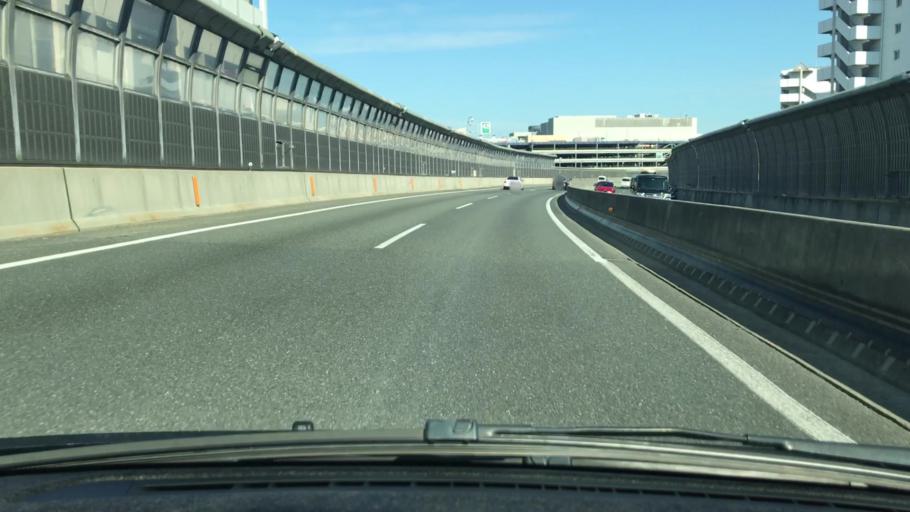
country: JP
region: Hyogo
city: Nishinomiya-hama
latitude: 34.7399
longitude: 135.3596
